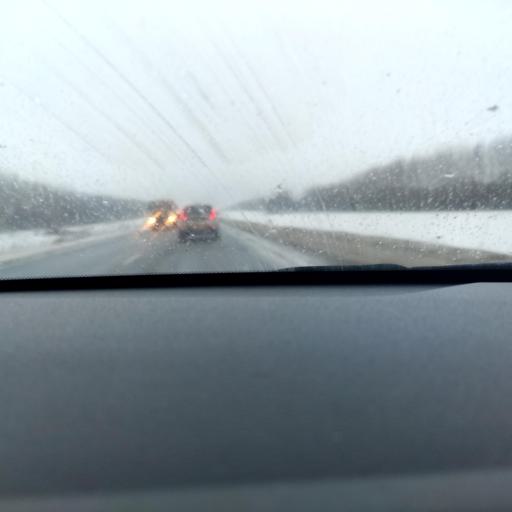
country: RU
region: Tatarstan
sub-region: Alekseyevskiy Rayon
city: Alekseyevskoye
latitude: 55.3111
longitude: 50.3760
